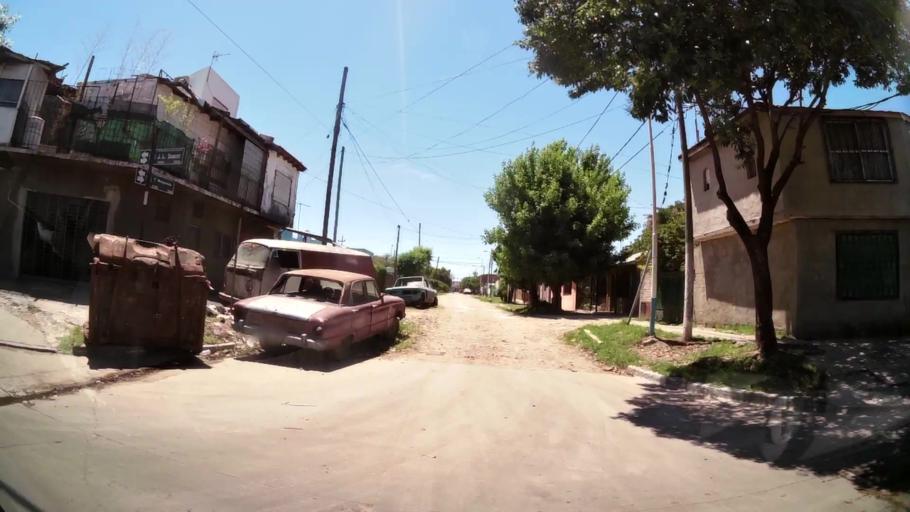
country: AR
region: Buenos Aires
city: Hurlingham
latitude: -34.5088
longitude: -58.7132
